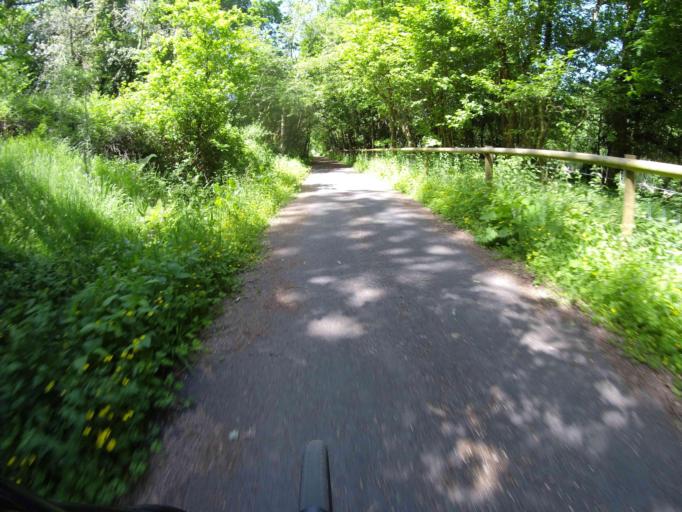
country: GB
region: England
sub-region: Devon
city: Bovey Tracey
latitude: 50.6415
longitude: -3.7372
